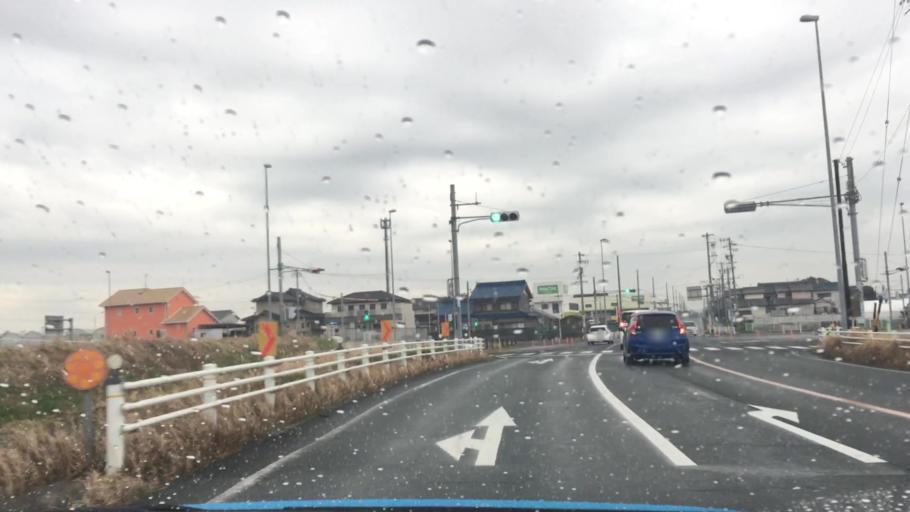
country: JP
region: Aichi
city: Toyohashi
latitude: 34.6965
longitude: 137.3908
